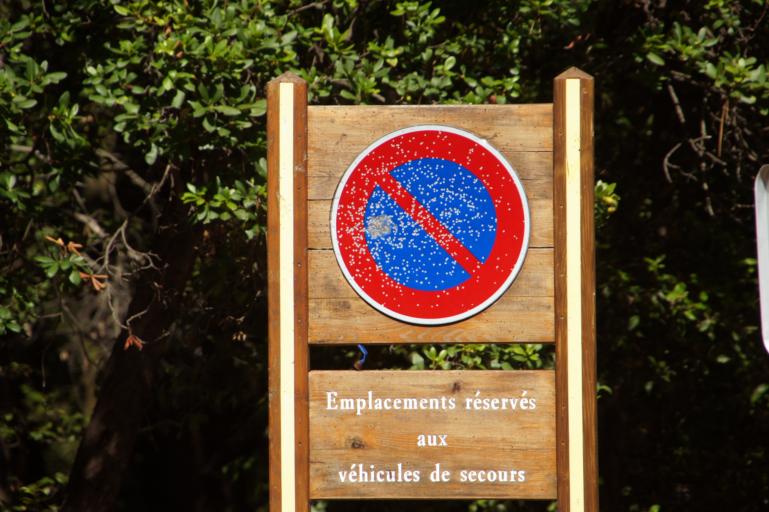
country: FR
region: Corsica
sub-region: Departement de la Corse-du-Sud
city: Cargese
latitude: 42.2526
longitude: 8.6575
